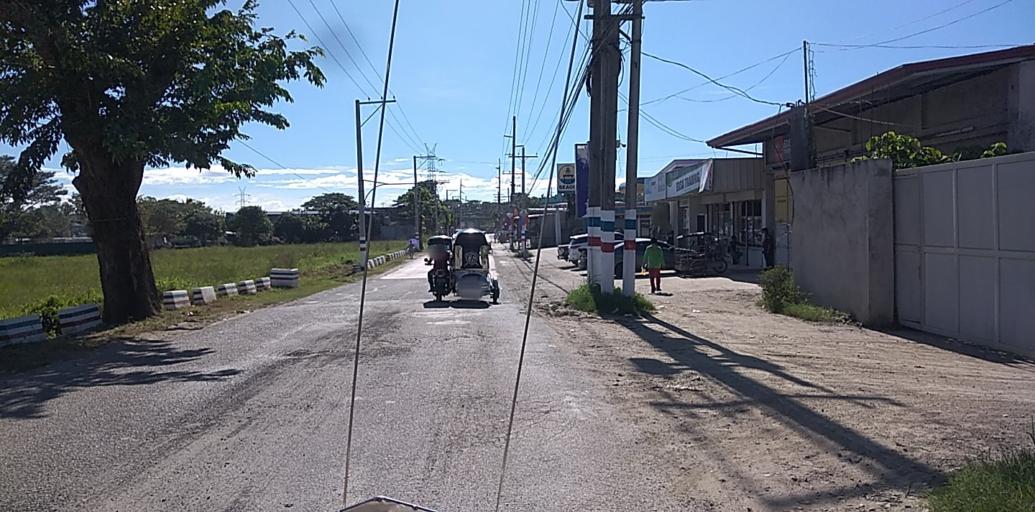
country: PH
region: Central Luzon
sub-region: Province of Pampanga
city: San Luis
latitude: 15.0446
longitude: 120.7881
